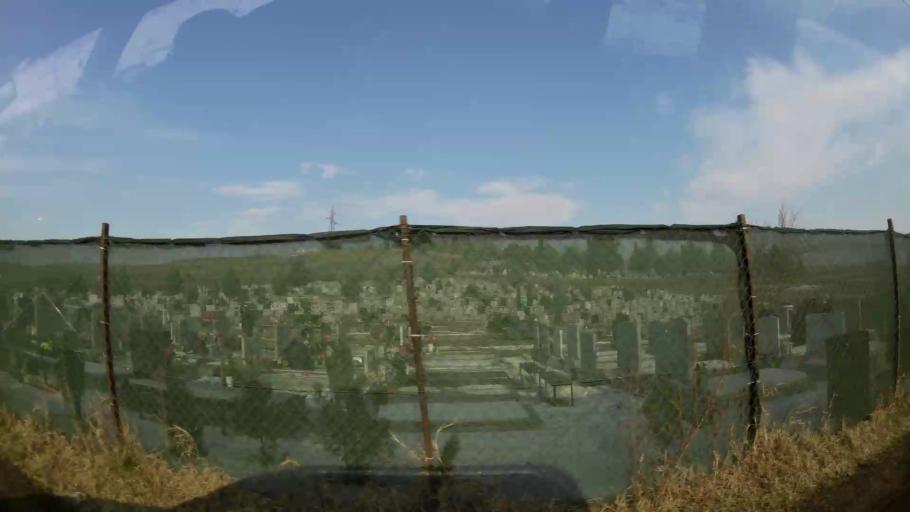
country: MK
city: Creshevo
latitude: 42.0149
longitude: 21.4915
